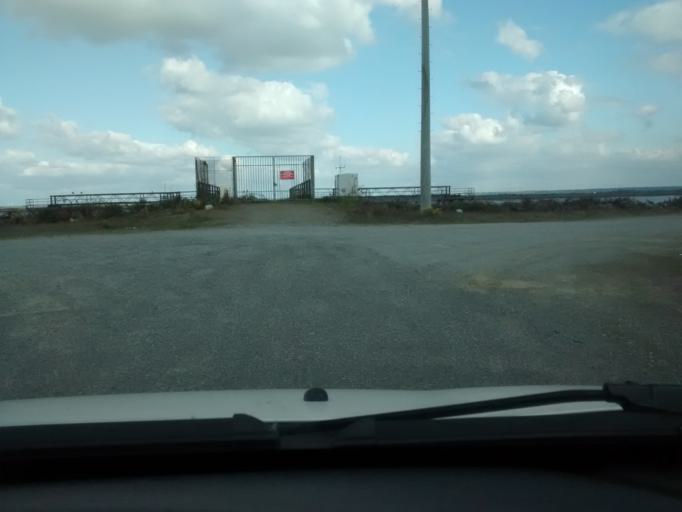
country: FR
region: Pays de la Loire
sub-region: Departement de la Loire-Atlantique
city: Saint-Paimboeuf
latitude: 47.2860
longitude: -2.0008
